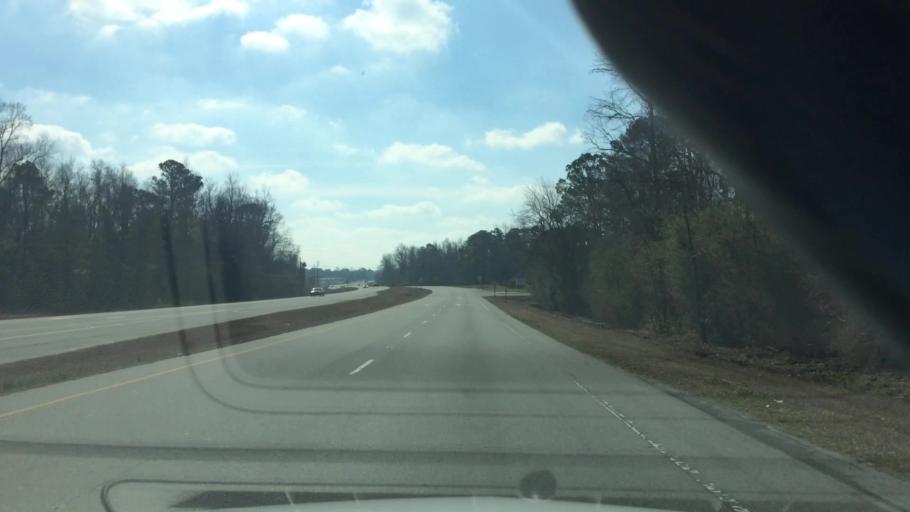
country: US
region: North Carolina
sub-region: Duplin County
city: Beulaville
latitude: 35.0868
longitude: -77.7302
